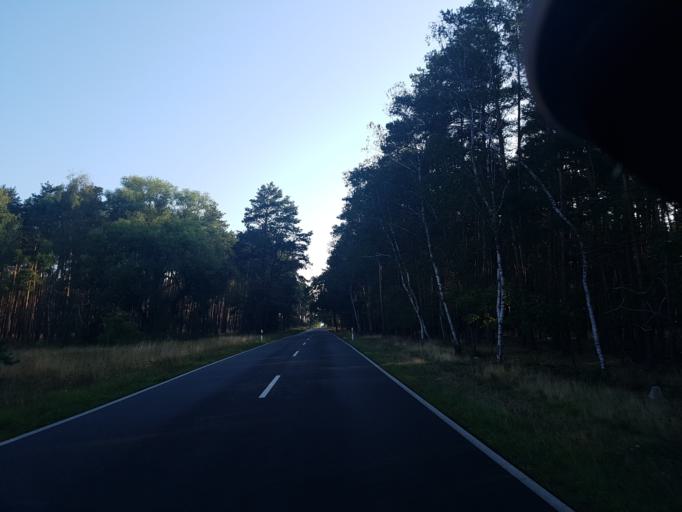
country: DE
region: Saxony-Anhalt
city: Holzdorf
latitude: 51.8037
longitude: 13.1372
